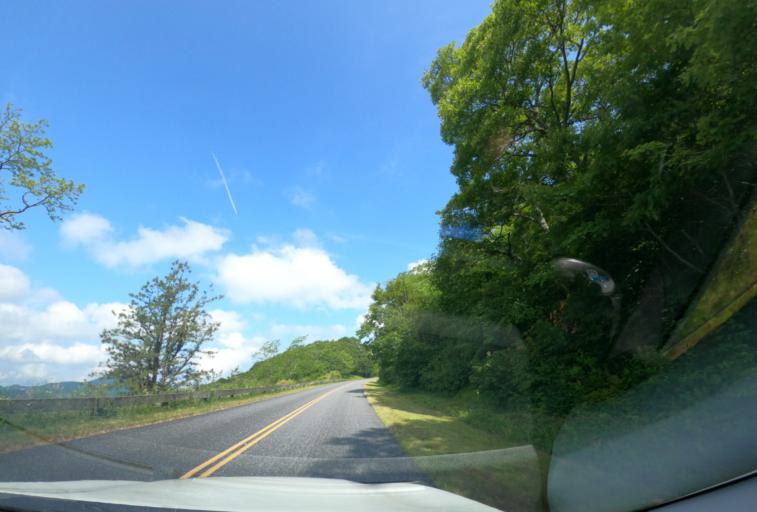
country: US
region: North Carolina
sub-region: Haywood County
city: Hazelwood
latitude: 35.3881
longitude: -83.0336
